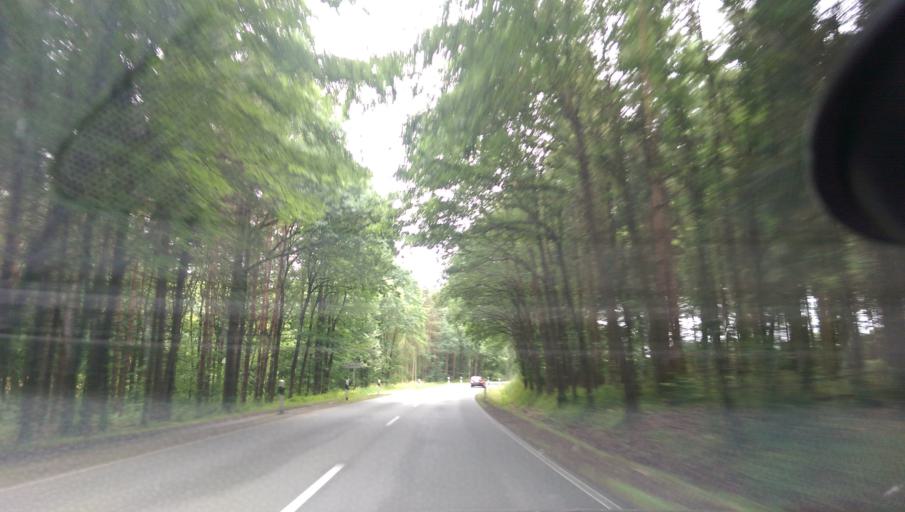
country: DE
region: Lower Saxony
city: Bad Fallingbostel
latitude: 52.8764
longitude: 9.6928
